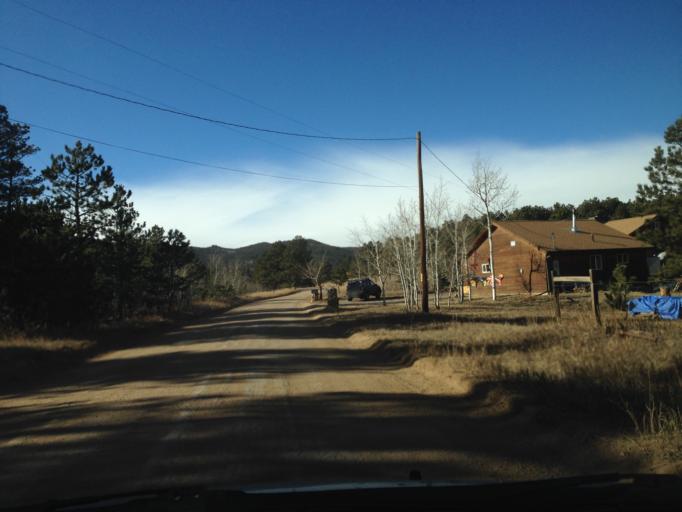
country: US
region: Colorado
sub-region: Boulder County
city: Coal Creek
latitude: 39.9137
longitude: -105.3525
